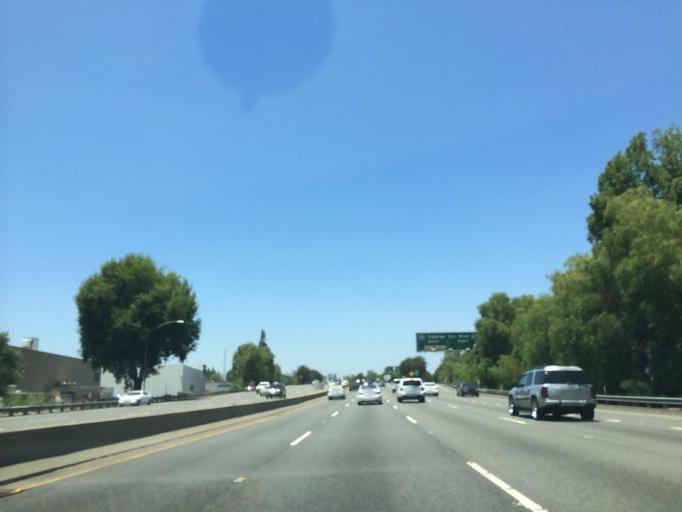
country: US
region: California
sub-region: Los Angeles County
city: Woodland Hills
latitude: 34.1701
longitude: -118.6016
